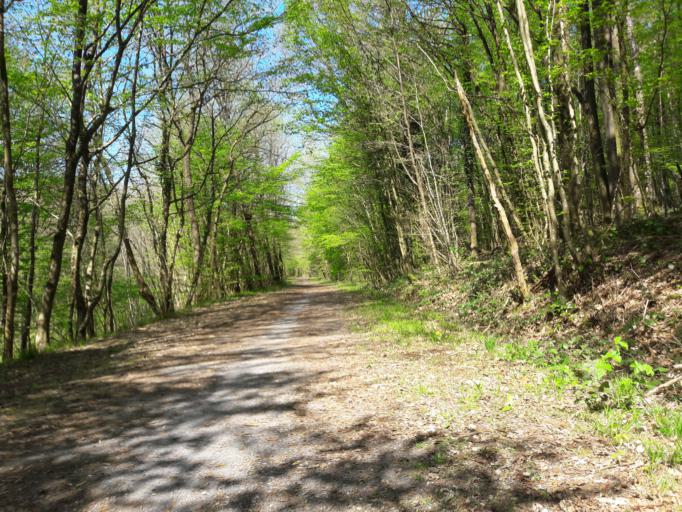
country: FR
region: Nord-Pas-de-Calais
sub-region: Departement du Nord
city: Sains-du-Nord
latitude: 50.1300
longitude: 4.0659
